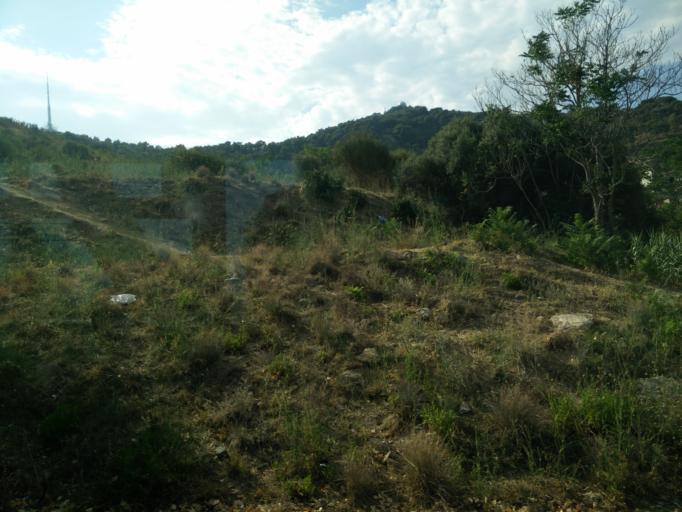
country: ES
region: Catalonia
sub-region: Provincia de Barcelona
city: Sarria-Sant Gervasi
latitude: 41.4132
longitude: 2.1293
